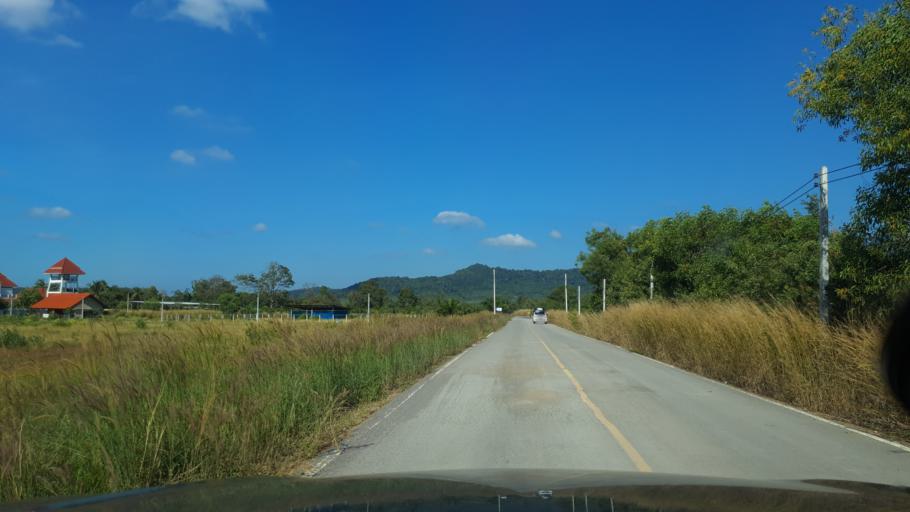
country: TH
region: Phangnga
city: Ban Ao Nang
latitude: 8.0511
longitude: 98.8015
